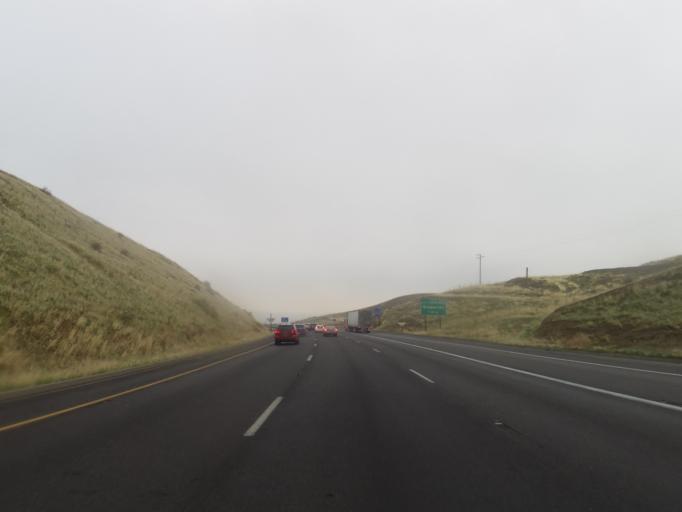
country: US
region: California
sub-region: Kern County
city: Lebec
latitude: 34.9274
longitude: -118.9223
